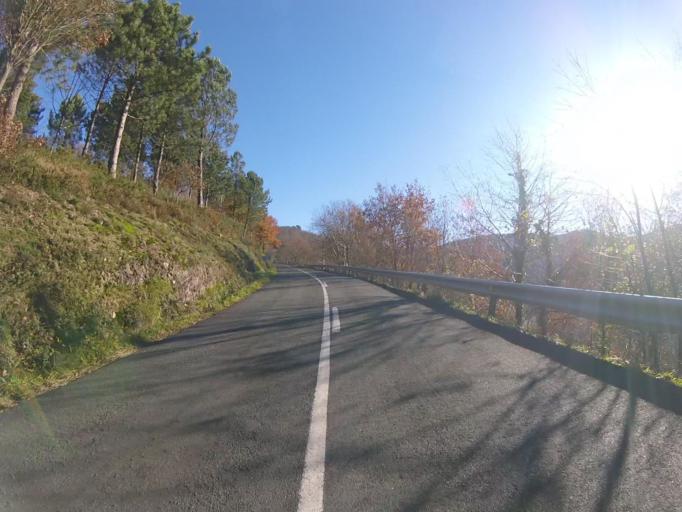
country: ES
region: Basque Country
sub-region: Provincia de Guipuzcoa
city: Irun
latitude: 43.3184
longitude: -1.7681
